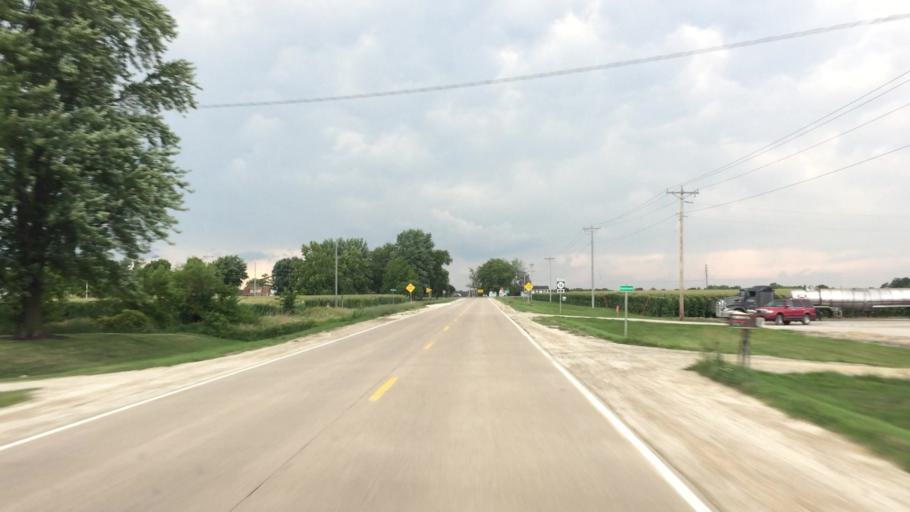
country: US
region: Iowa
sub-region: Lee County
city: Fort Madison
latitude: 40.7385
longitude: -91.3282
